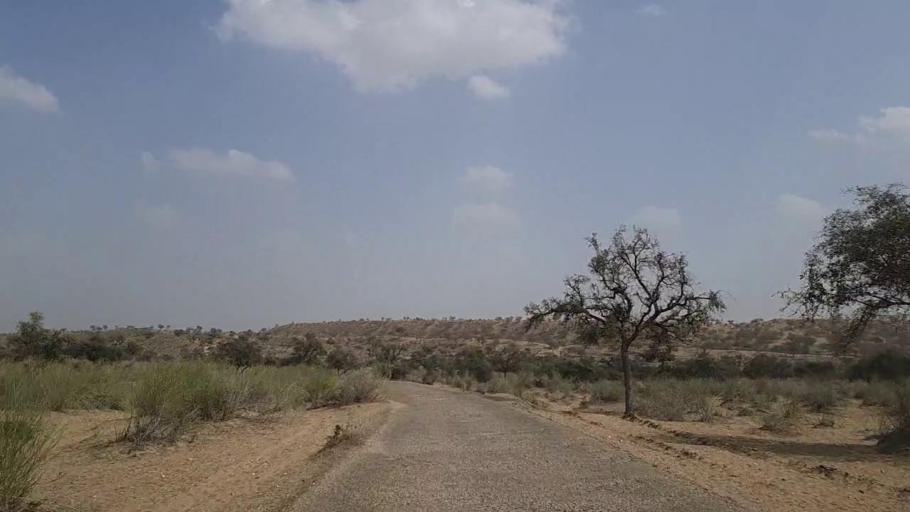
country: PK
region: Sindh
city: Islamkot
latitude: 24.7869
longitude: 70.0907
